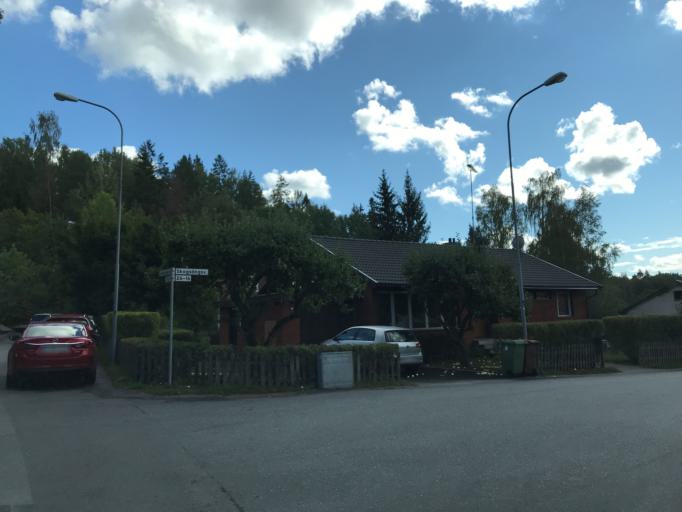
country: SE
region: Stockholm
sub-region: Sollentuna Kommun
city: Sollentuna
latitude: 59.4521
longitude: 17.9616
